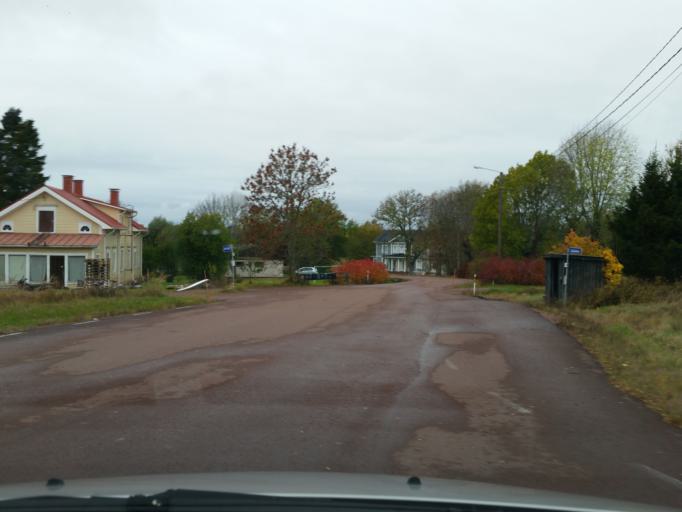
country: AX
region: Alands landsbygd
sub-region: Lemland
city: Lemland
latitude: 60.0717
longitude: 20.0848
